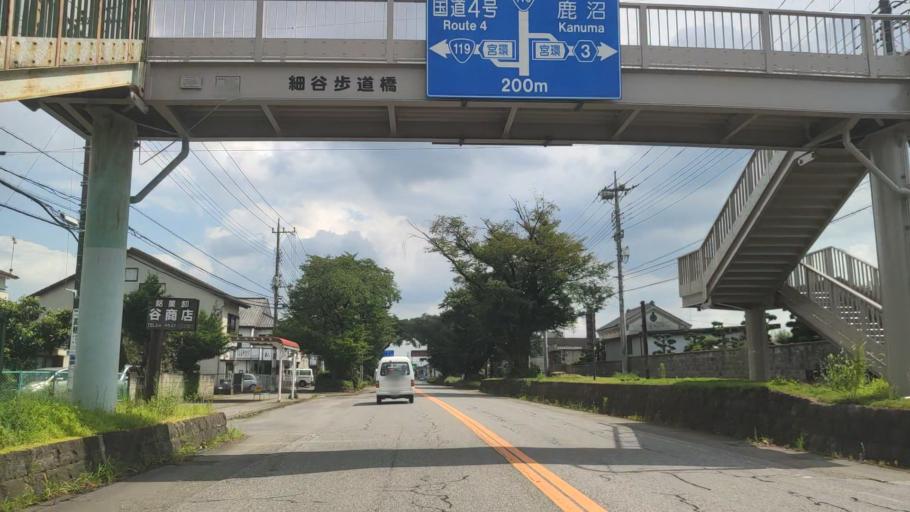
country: JP
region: Tochigi
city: Utsunomiya-shi
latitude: 36.5930
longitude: 139.8621
